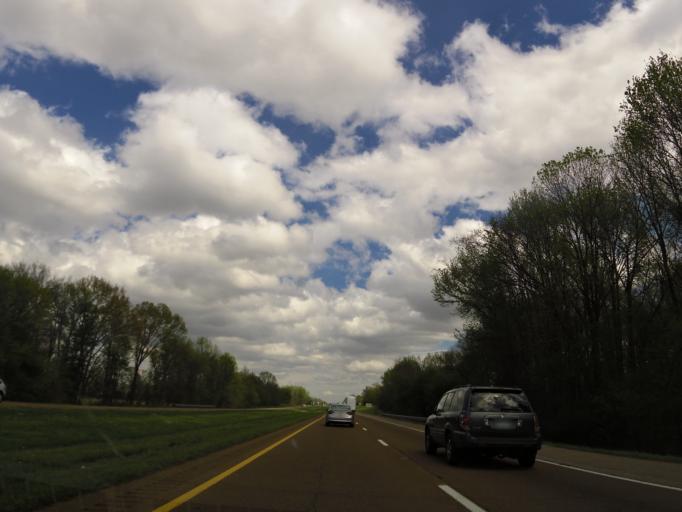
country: US
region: Tennessee
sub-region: Tipton County
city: Mason
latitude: 35.3765
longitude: -89.4533
